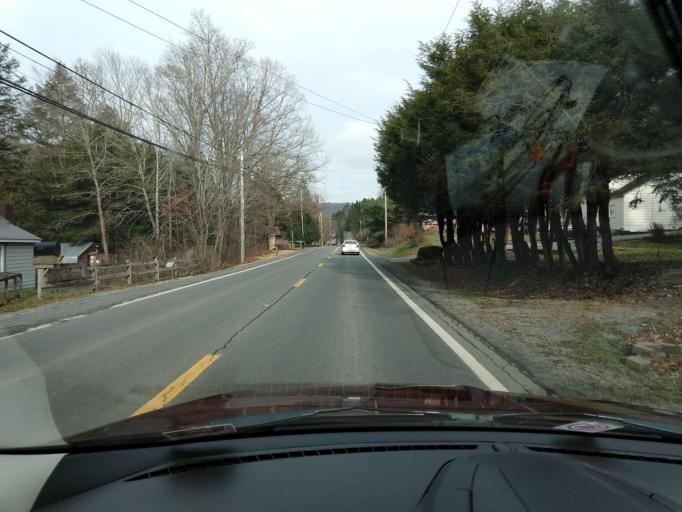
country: US
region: West Virginia
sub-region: Greenbrier County
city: Rainelle
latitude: 37.9928
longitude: -80.7340
